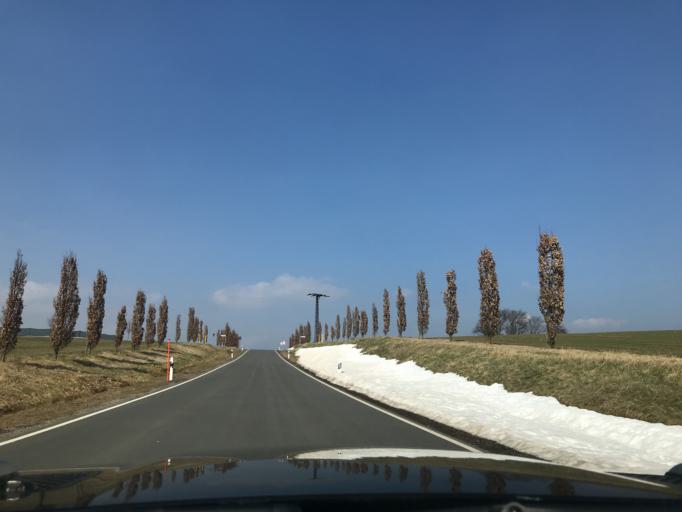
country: DE
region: Thuringia
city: Flarchheim
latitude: 51.1294
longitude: 10.4737
